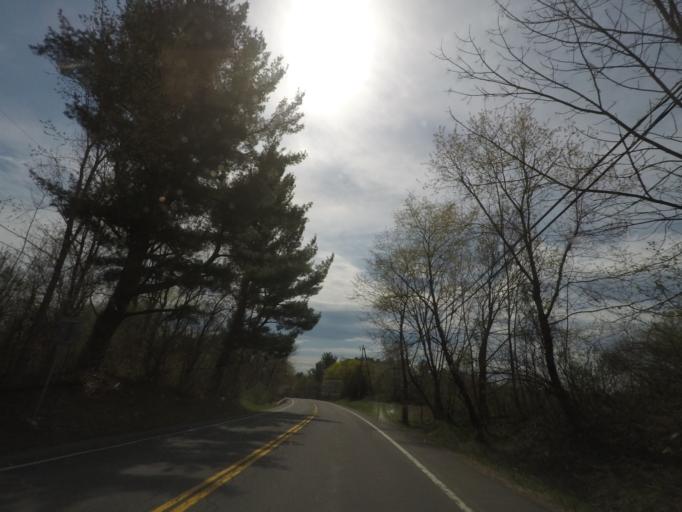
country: US
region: New York
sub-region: Columbia County
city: Chatham
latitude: 42.3216
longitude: -73.6245
